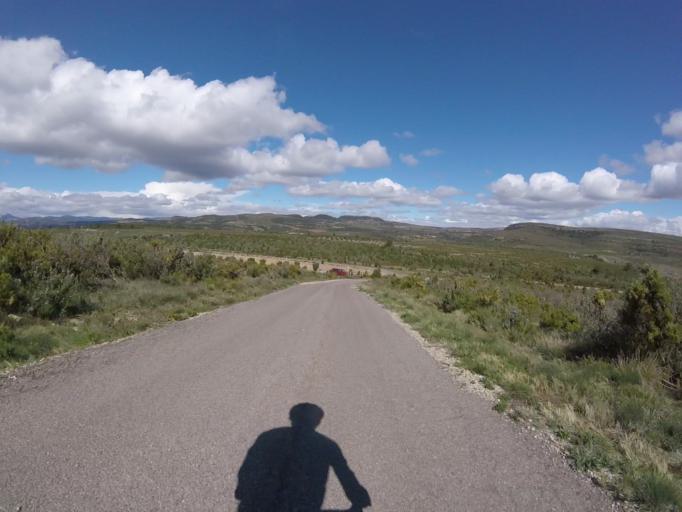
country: ES
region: Valencia
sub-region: Provincia de Castello
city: Culla
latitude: 40.3061
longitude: -0.1172
